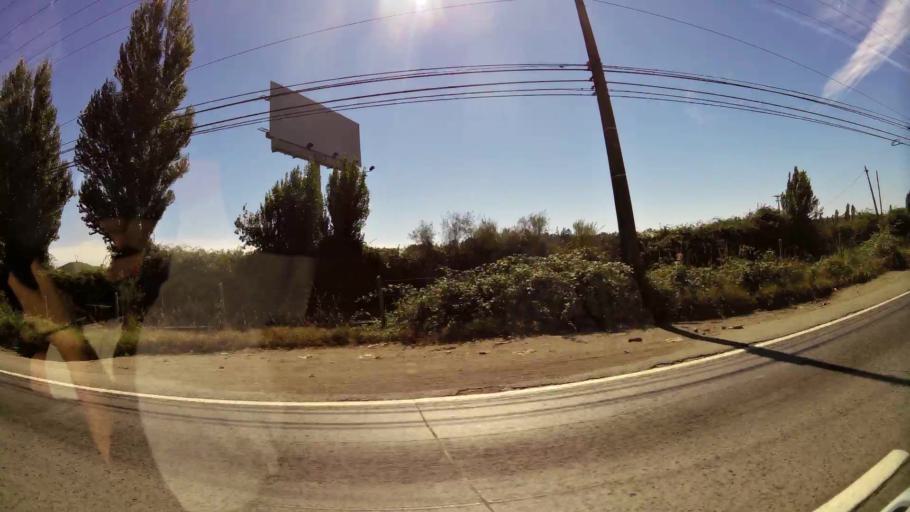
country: CL
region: Biobio
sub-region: Provincia de Concepcion
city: Concepcion
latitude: -36.7899
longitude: -73.0245
